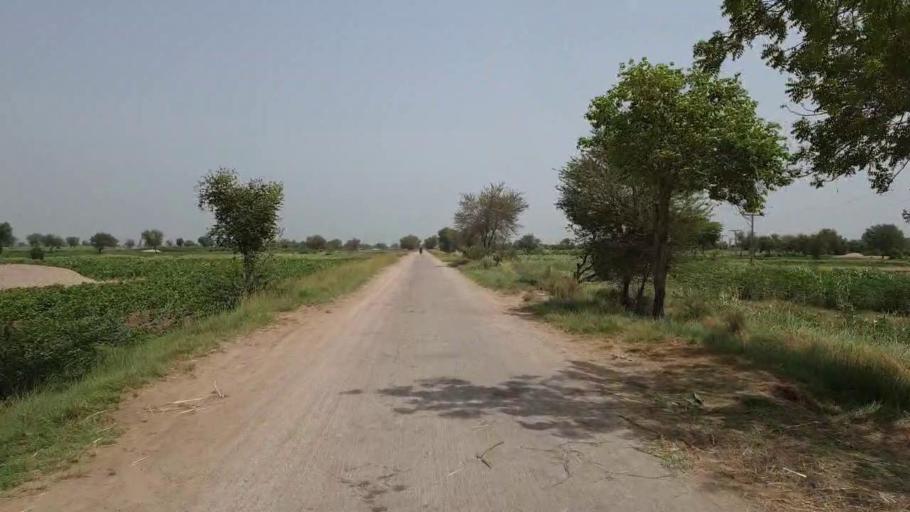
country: PK
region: Sindh
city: Nawabshah
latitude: 26.2601
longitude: 68.3192
